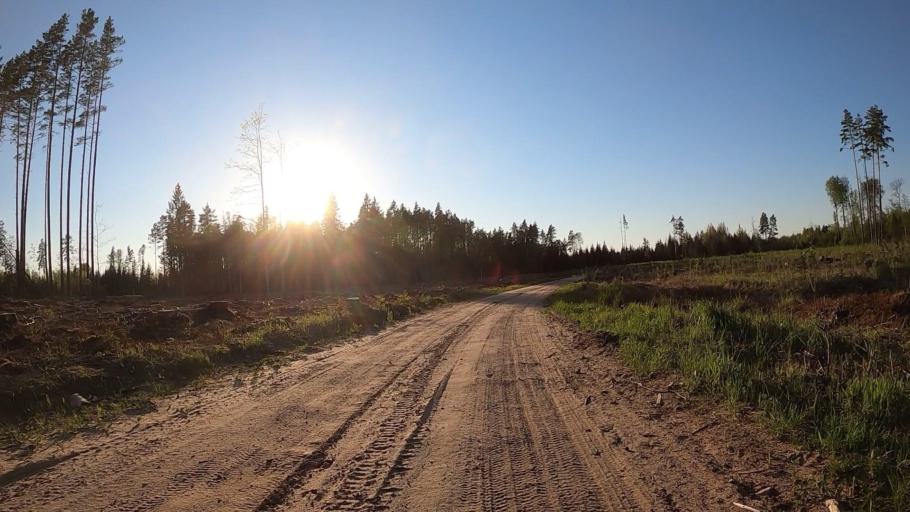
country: LV
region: Kekava
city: Kekava
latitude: 56.7772
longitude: 24.2158
